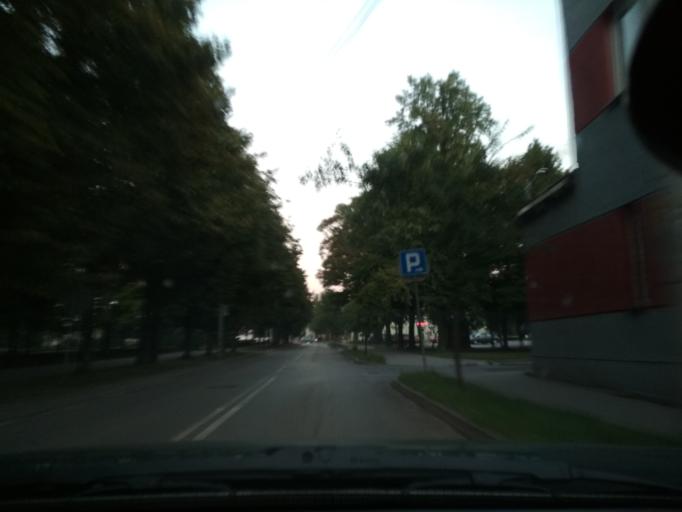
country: PL
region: Silesian Voivodeship
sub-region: Powiat zawiercianski
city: Zawiercie
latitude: 50.4866
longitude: 19.4309
